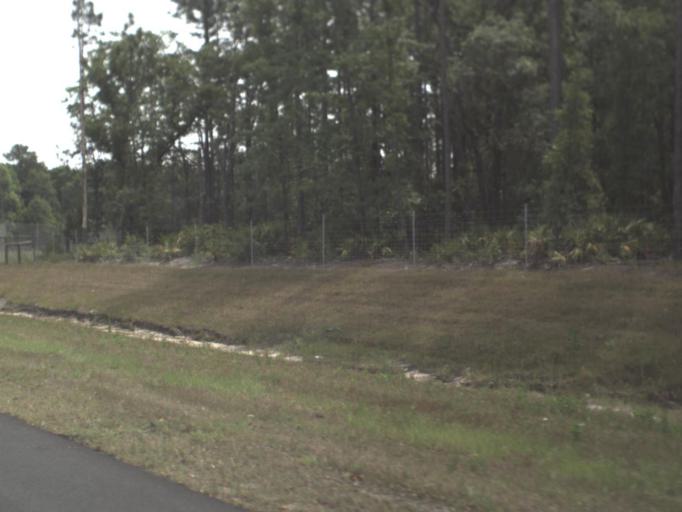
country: US
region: Florida
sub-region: Nassau County
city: Nassau Village-Ratliff
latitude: 30.4740
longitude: -81.9063
